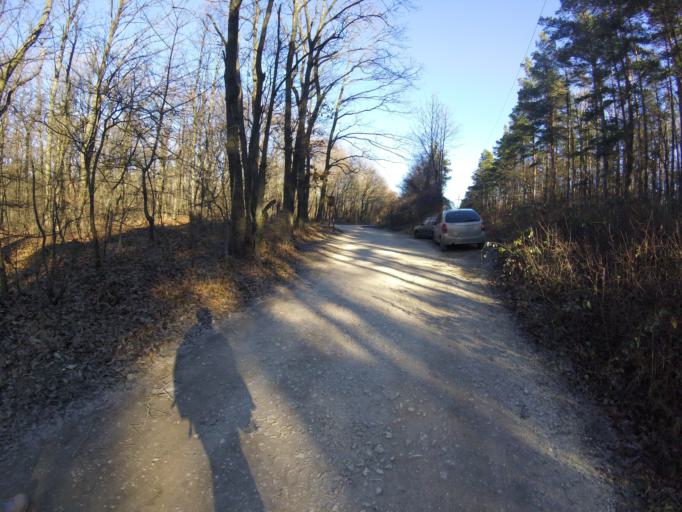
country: HU
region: Pest
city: Pilisszanto
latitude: 47.6801
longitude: 18.8940
